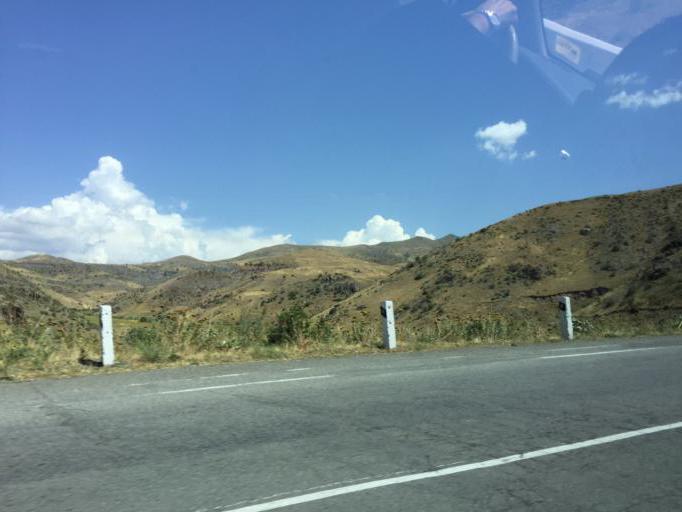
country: AM
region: Vayots' Dzori Marz
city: Jermuk
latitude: 39.7219
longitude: 45.6385
